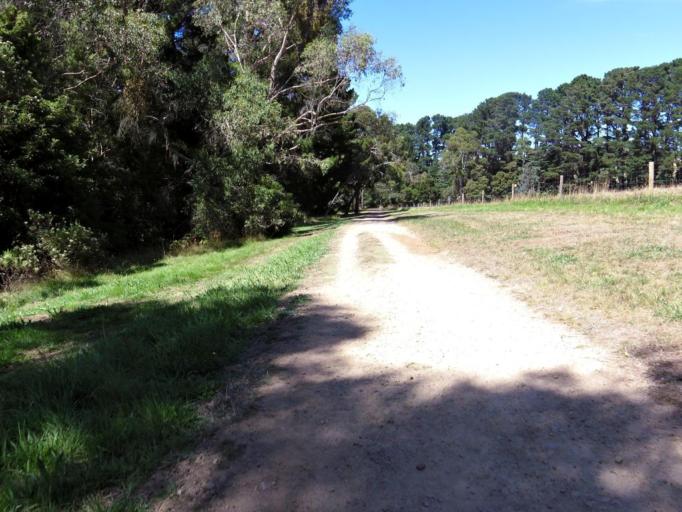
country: AU
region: Victoria
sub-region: Mornington Peninsula
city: Merricks
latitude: -38.3820
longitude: 145.0603
